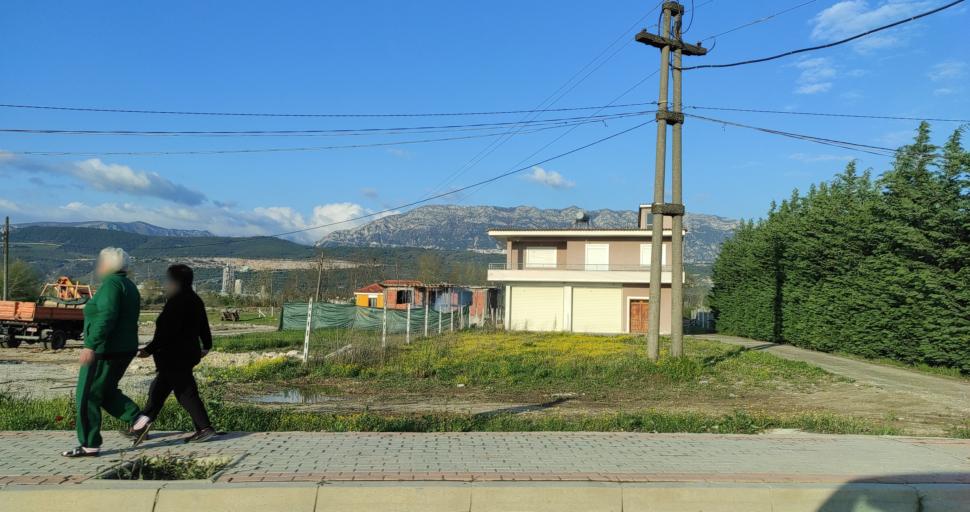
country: AL
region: Durres
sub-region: Rrethi i Krujes
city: Fushe-Kruje
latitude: 41.4880
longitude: 19.7256
